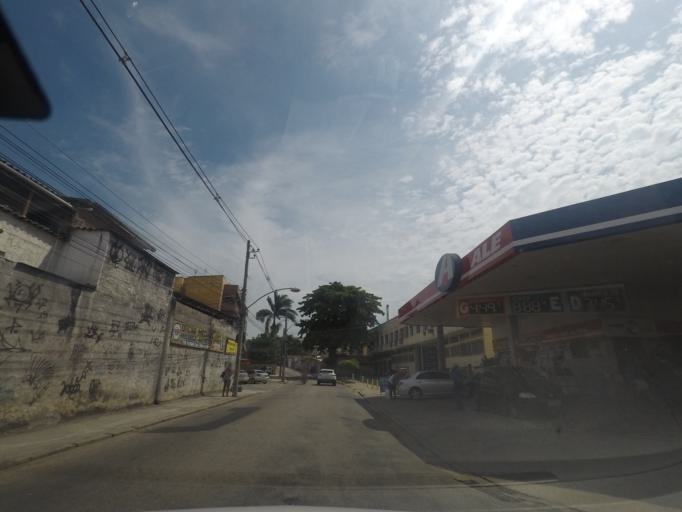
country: BR
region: Rio de Janeiro
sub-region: Rio De Janeiro
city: Rio de Janeiro
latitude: -22.8186
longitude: -43.1882
